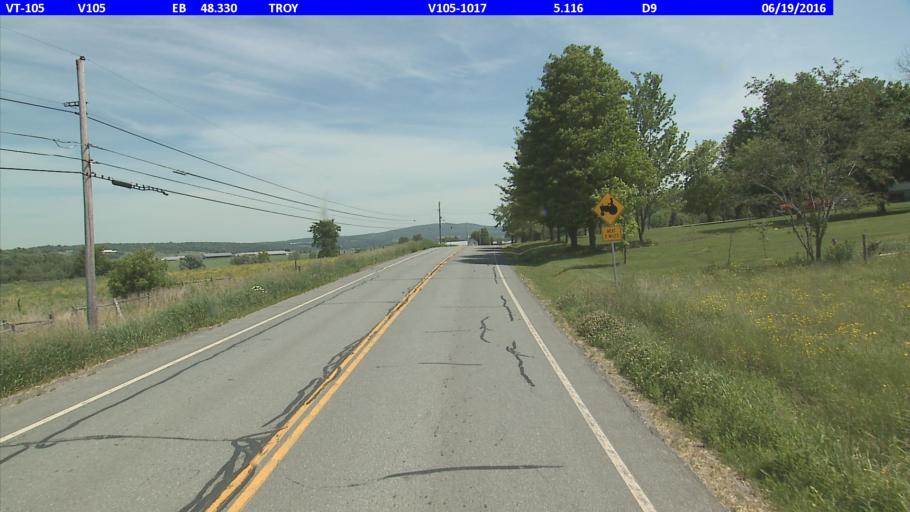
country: US
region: Vermont
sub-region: Orleans County
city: Newport
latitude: 44.9838
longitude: -72.3587
